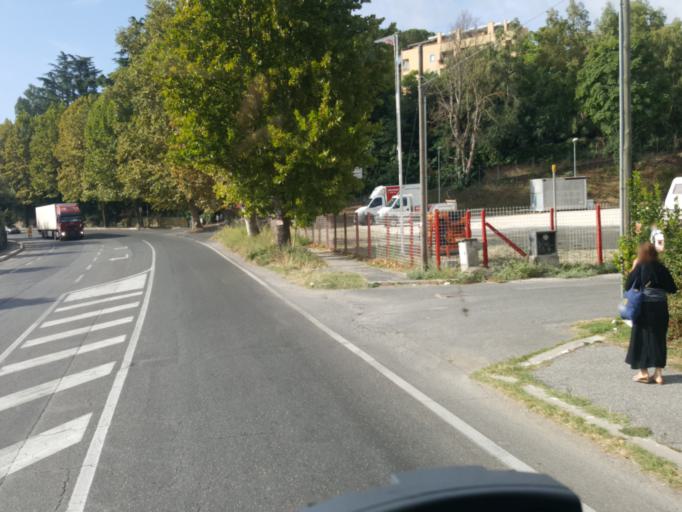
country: IT
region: Latium
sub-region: Citta metropolitana di Roma Capitale
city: Girardi-Bellavista-Terrazze
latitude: 42.1057
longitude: 12.5828
